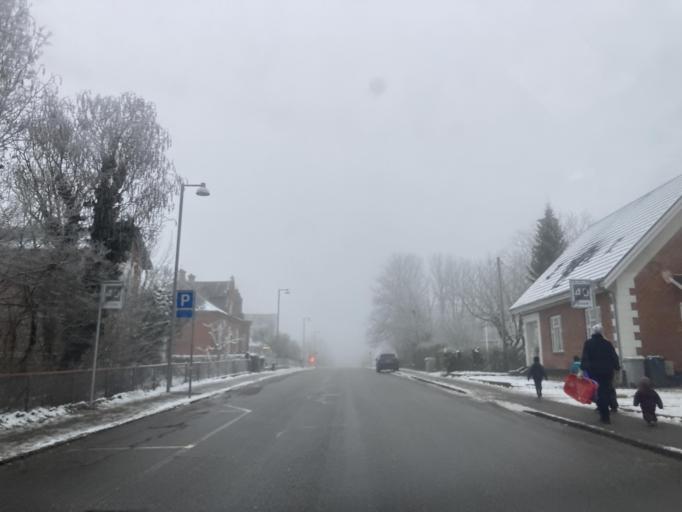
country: DK
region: Zealand
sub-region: Soro Kommune
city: Stenlille
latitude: 55.5409
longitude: 11.5925
